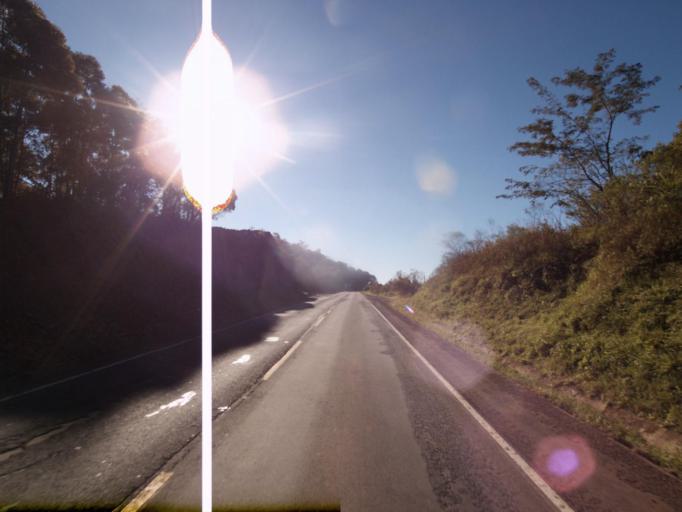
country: AR
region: Misiones
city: Bernardo de Irigoyen
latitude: -26.4914
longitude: -53.5027
